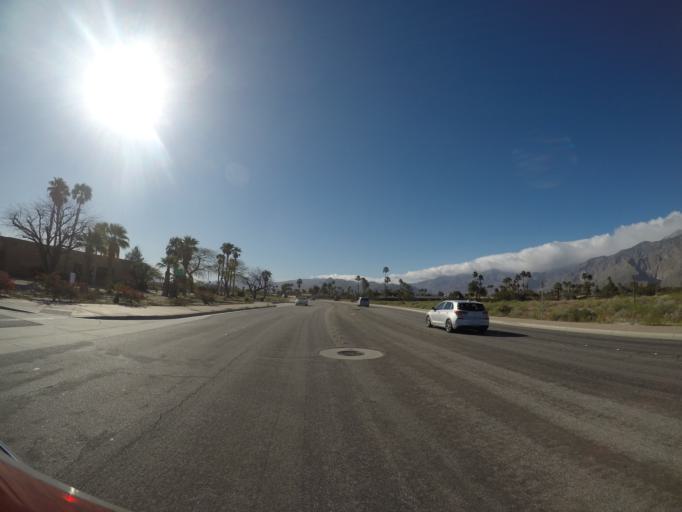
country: US
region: California
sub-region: Riverside County
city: Palm Springs
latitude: 33.8371
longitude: -116.5197
